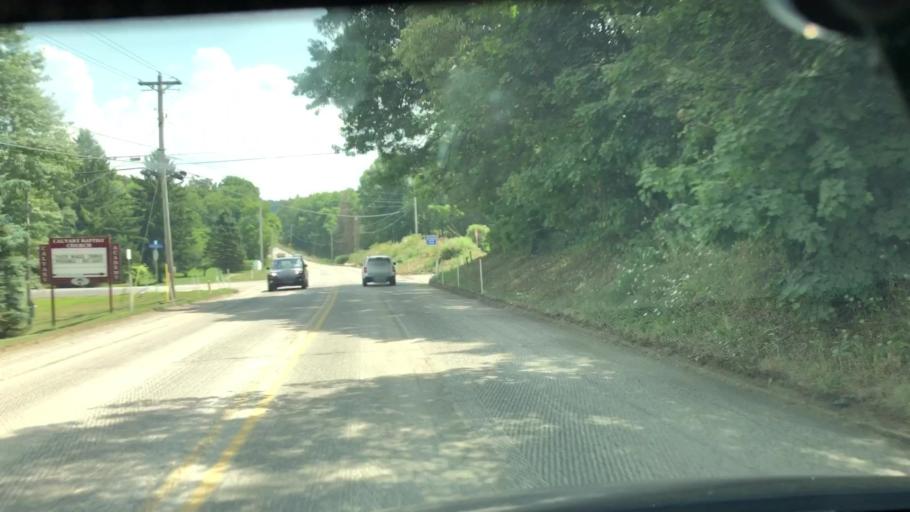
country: US
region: Pennsylvania
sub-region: Butler County
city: Saxonburg
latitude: 40.7981
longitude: -79.8214
